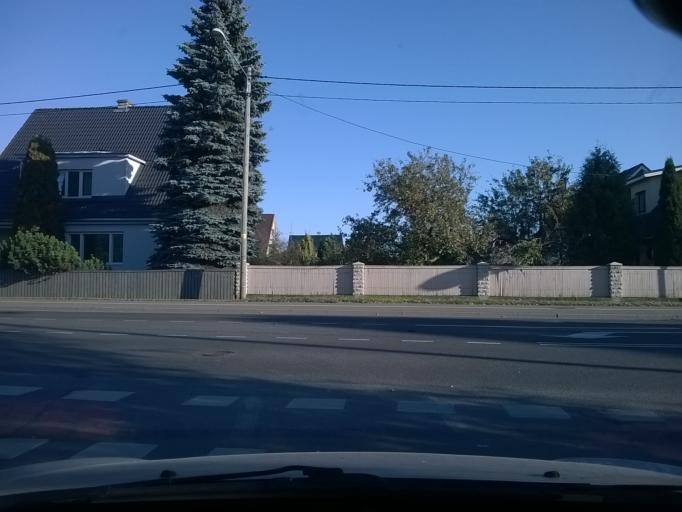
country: EE
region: Tartu
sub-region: Tartu linn
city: Tartu
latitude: 58.3484
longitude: 26.7163
